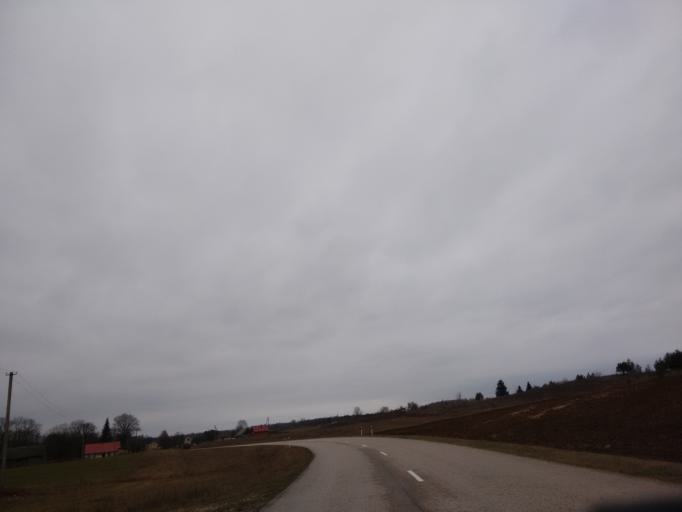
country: LT
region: Alytaus apskritis
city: Druskininkai
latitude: 54.2249
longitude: 23.8922
